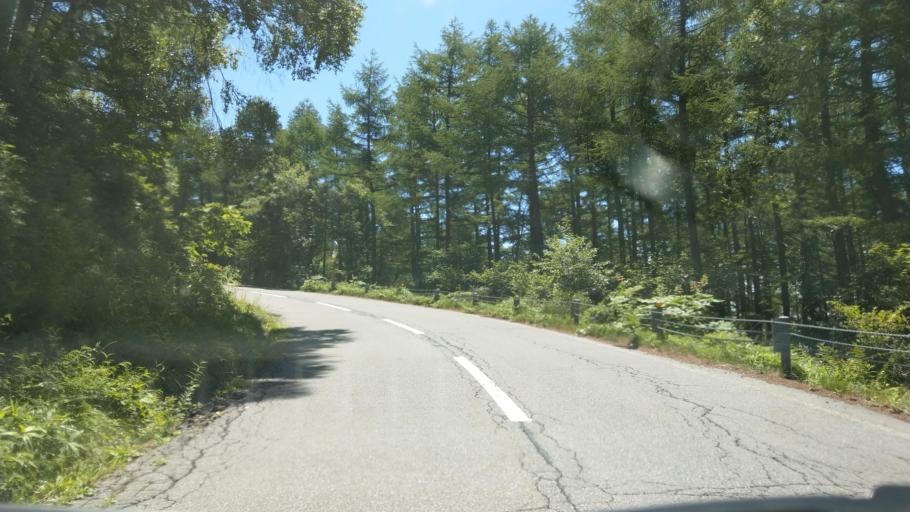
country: JP
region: Nagano
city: Komoro
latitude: 36.3948
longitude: 138.4712
